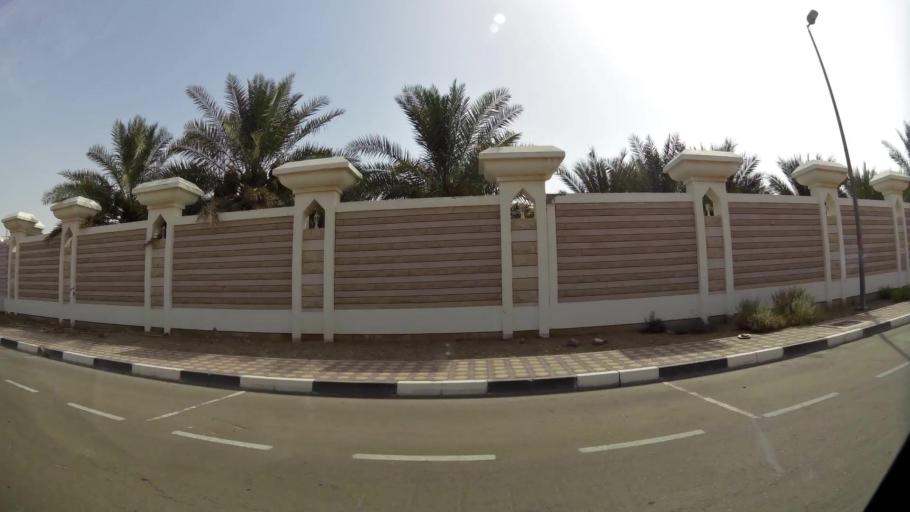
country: AE
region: Abu Dhabi
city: Al Ain
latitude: 24.1654
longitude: 55.7049
